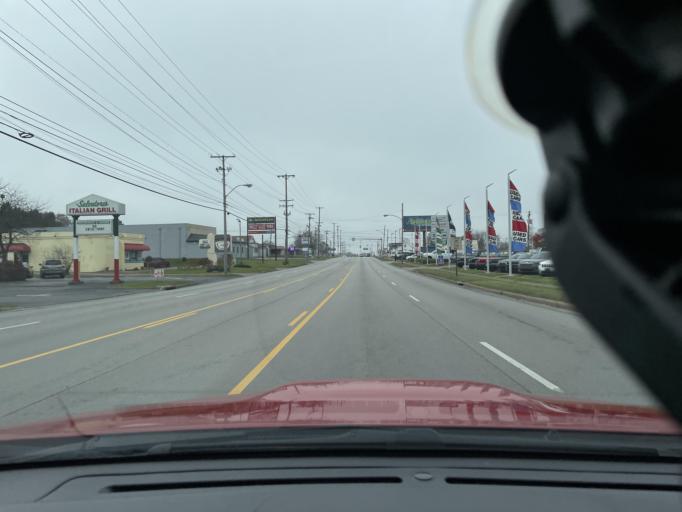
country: US
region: Ohio
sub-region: Mahoning County
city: Austintown
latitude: 41.1005
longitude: -80.7455
